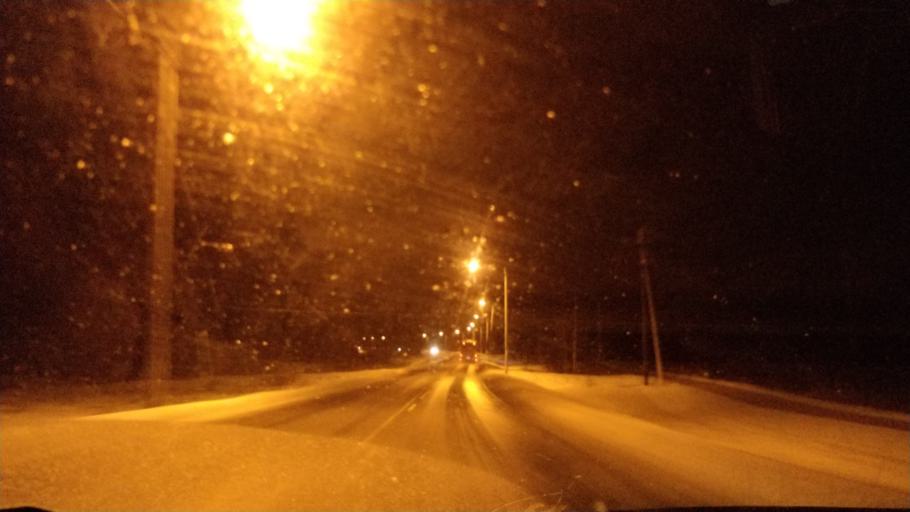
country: FI
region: Lapland
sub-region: Rovaniemi
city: Rovaniemi
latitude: 66.2880
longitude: 25.3462
